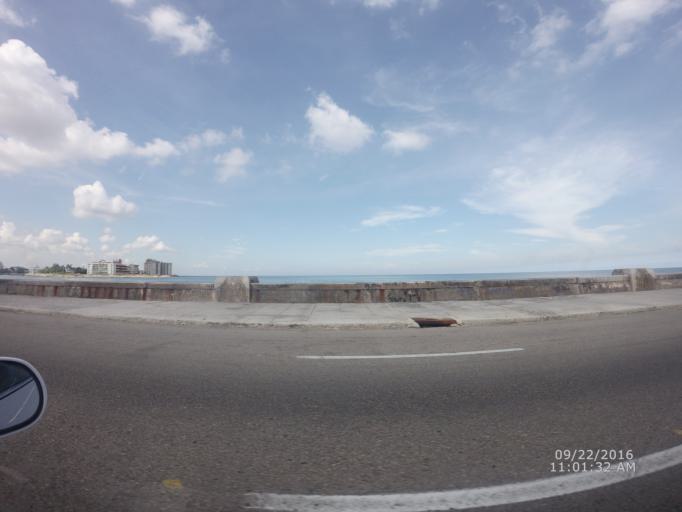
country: CU
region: La Habana
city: Havana
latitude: 23.1364
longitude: -82.4082
